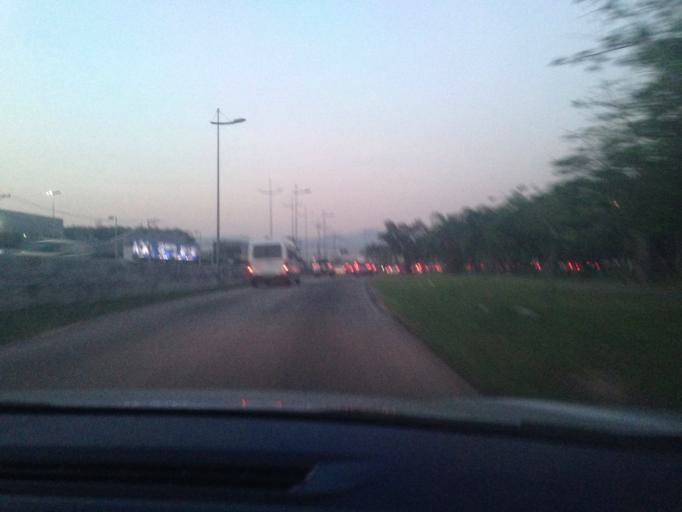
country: BR
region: Rio de Janeiro
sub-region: Sao Joao De Meriti
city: Sao Joao de Meriti
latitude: -22.9728
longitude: -43.3626
